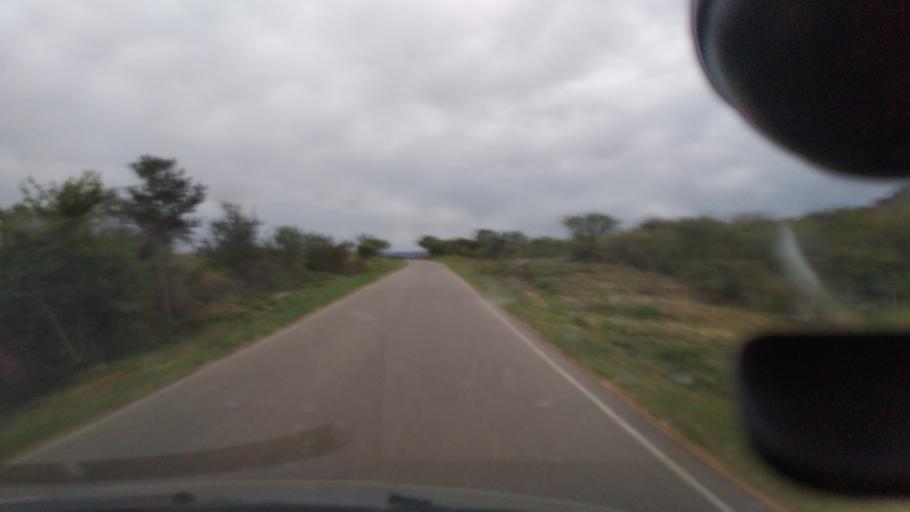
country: AR
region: Cordoba
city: Villa Las Rosas
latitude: -31.8852
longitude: -65.0259
